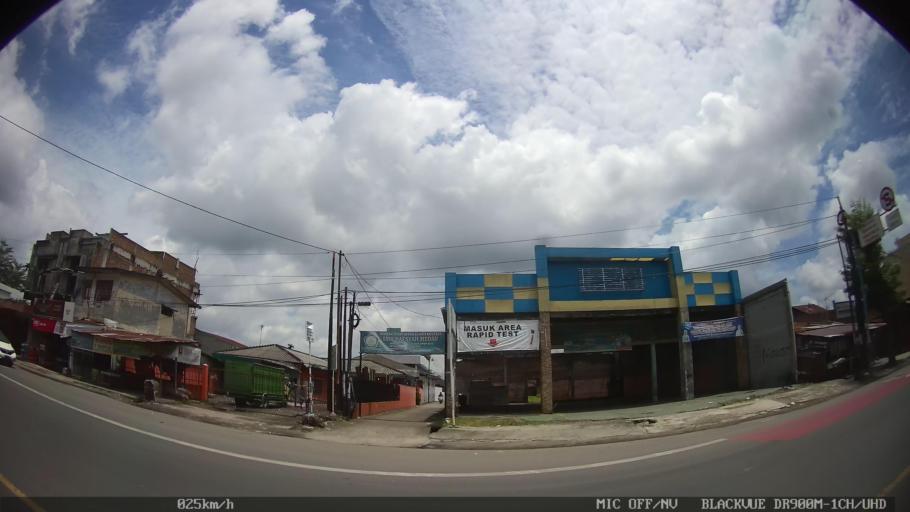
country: ID
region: North Sumatra
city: Medan
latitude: 3.5972
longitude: 98.7273
